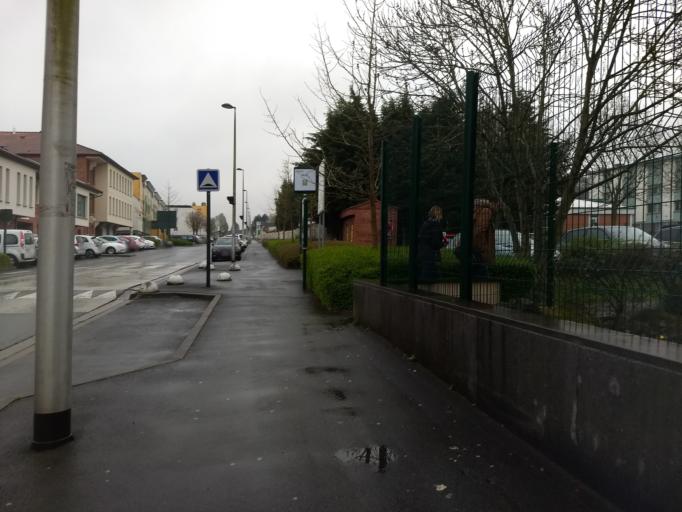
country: FR
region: Nord-Pas-de-Calais
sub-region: Departement du Pas-de-Calais
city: Lievin
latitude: 50.4243
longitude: 2.7928
